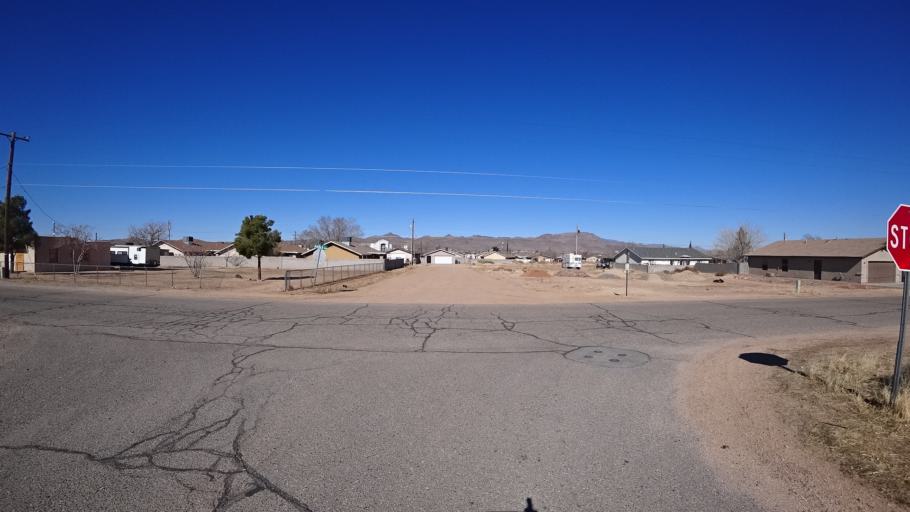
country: US
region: Arizona
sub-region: Mohave County
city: Kingman
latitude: 35.2057
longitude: -114.0233
